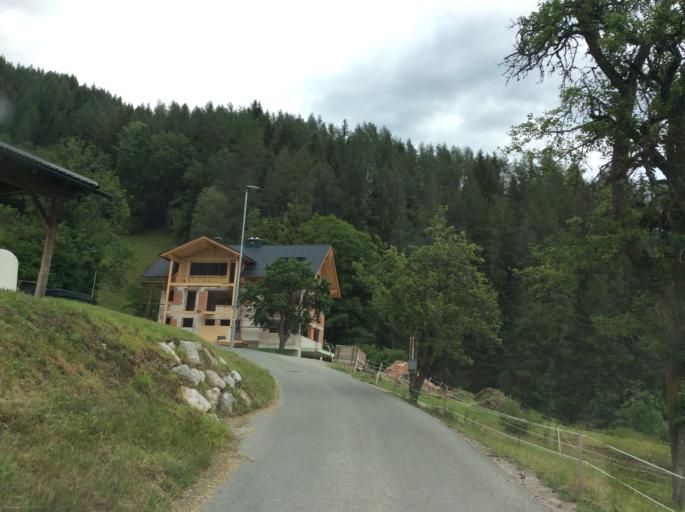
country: AT
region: Styria
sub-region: Politischer Bezirk Liezen
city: Schladming
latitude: 47.4039
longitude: 13.6976
